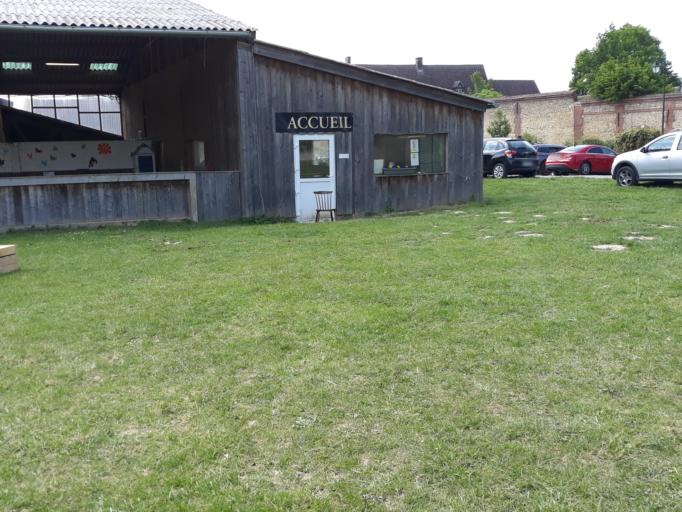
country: FR
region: Picardie
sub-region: Departement de l'Oise
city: Saint-Crepin-Ibouvillers
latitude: 49.2743
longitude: 2.0368
